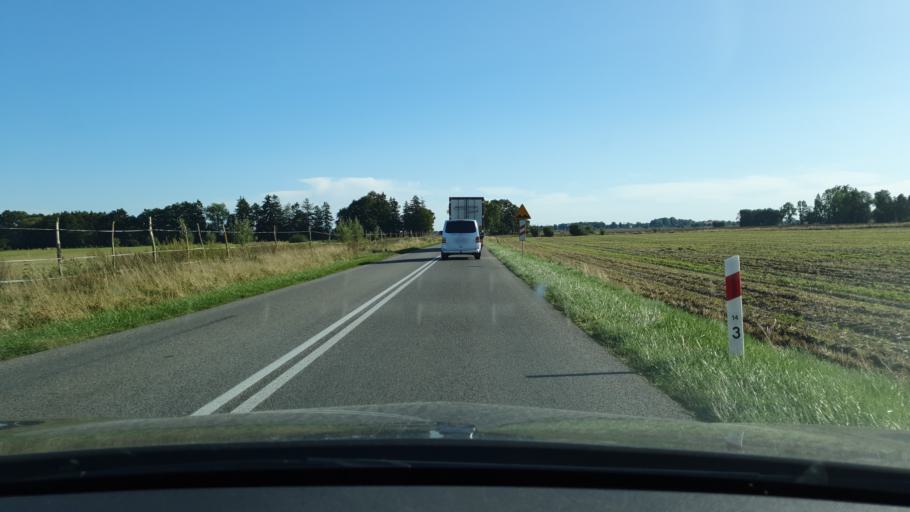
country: PL
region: West Pomeranian Voivodeship
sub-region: Powiat kamienski
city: Golczewo
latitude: 53.8290
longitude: 14.9282
